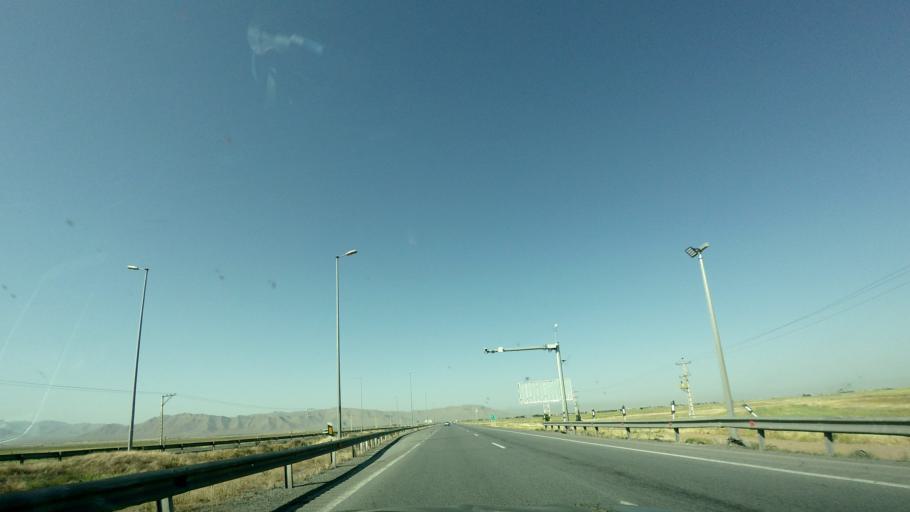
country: IR
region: Markazi
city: Ashtian
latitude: 34.1833
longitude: 50.0479
